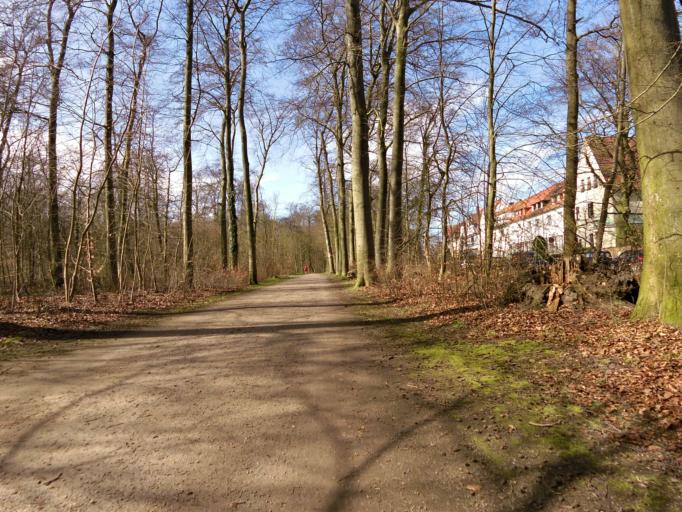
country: DE
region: Lower Saxony
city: Laatzen
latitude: 52.3692
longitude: 9.7924
